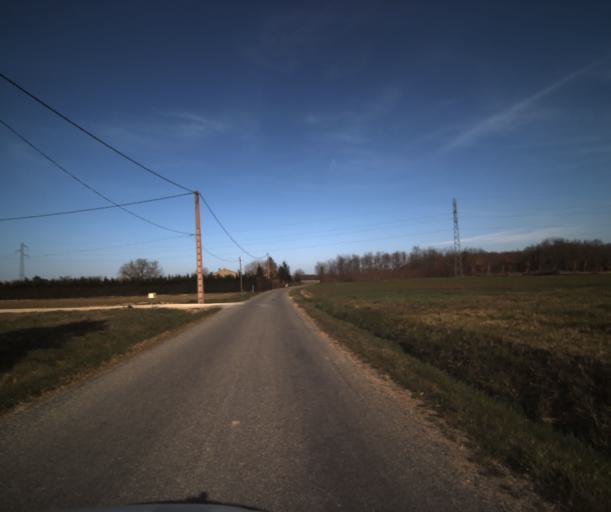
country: FR
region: Midi-Pyrenees
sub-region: Departement du Tarn-et-Garonne
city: Campsas
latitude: 43.9123
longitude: 1.3315
